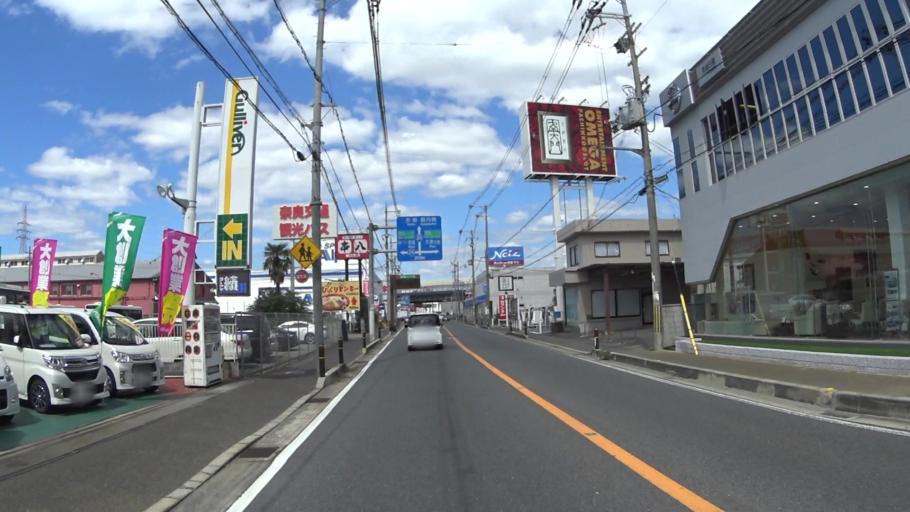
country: JP
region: Kyoto
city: Uji
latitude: 34.9066
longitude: 135.7838
